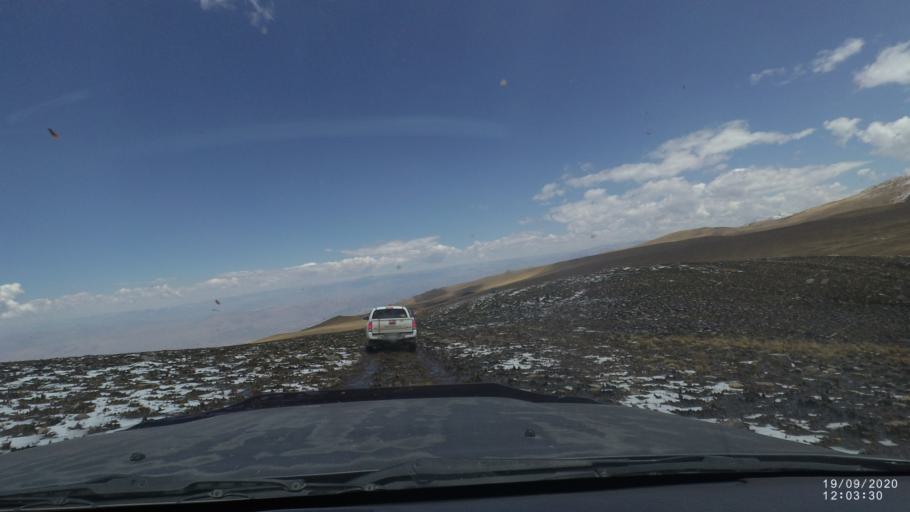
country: BO
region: Cochabamba
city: Cochabamba
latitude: -17.2988
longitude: -66.1060
